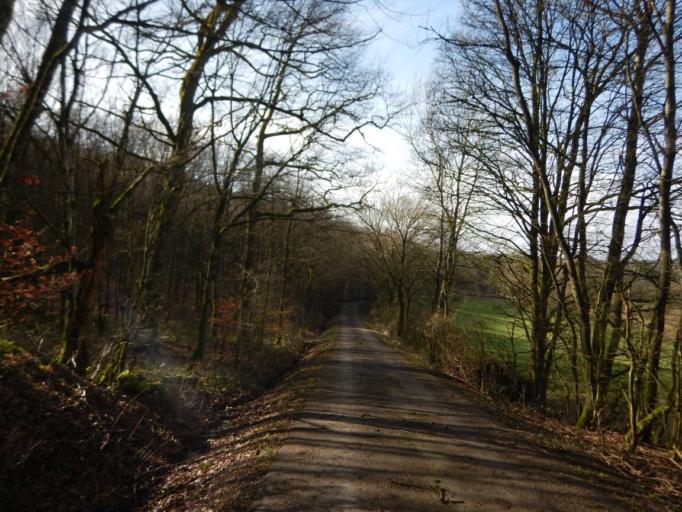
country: LU
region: Grevenmacher
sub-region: Canton d'Echternach
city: Mompach
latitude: 49.7667
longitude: 6.4332
